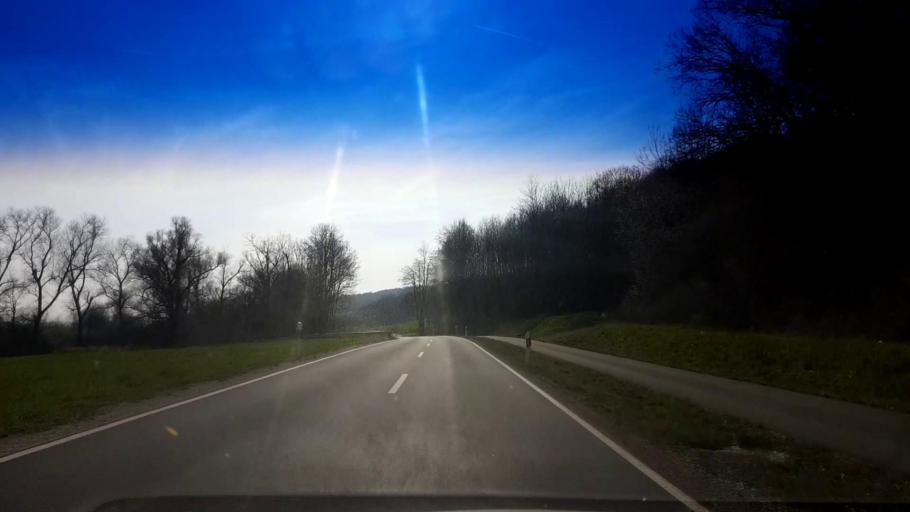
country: DE
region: Bavaria
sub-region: Upper Franconia
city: Ebensfeld
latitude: 50.0584
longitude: 10.9380
